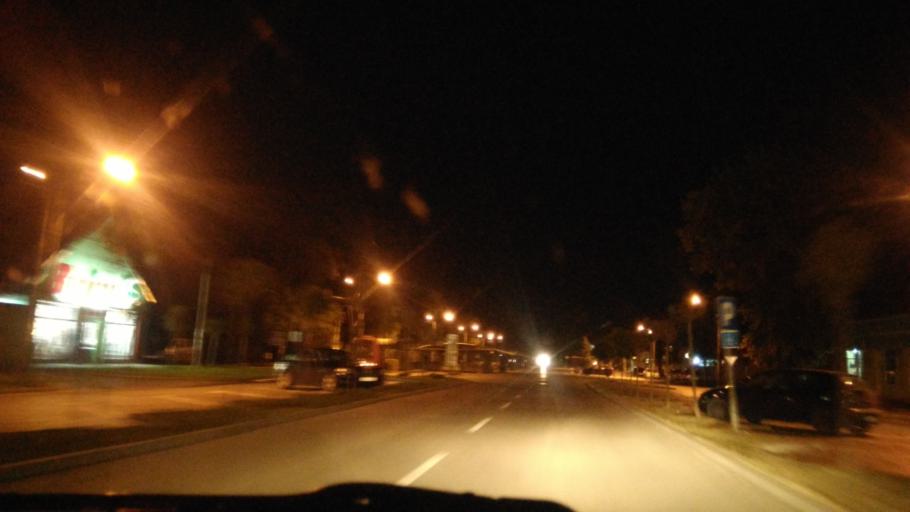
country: RS
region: Autonomna Pokrajina Vojvodina
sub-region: Juznobacki Okrug
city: Temerin
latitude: 45.4077
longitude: 19.8864
